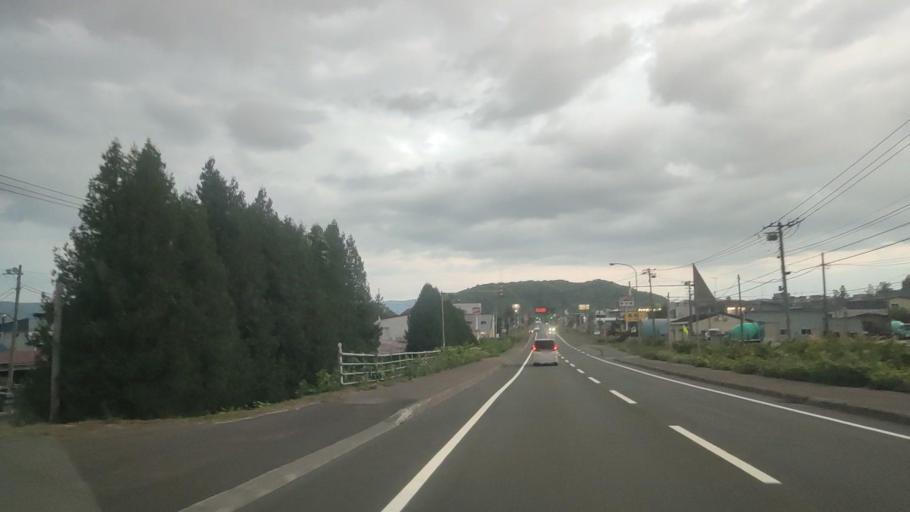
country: JP
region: Hokkaido
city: Shimo-furano
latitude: 43.3514
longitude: 142.3664
